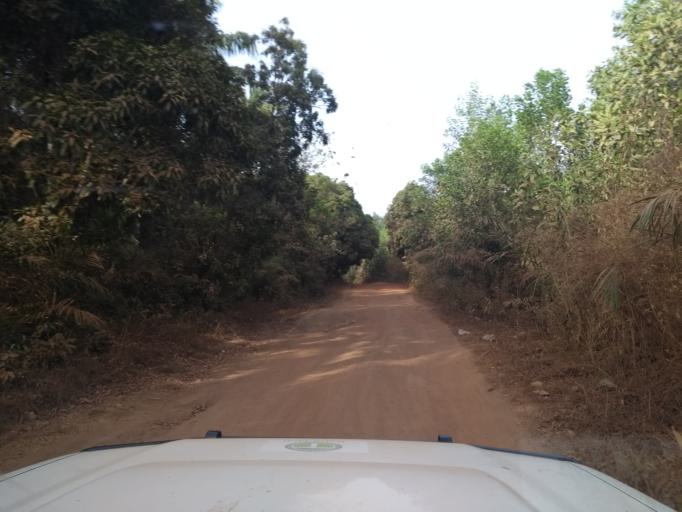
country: GN
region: Kindia
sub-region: Prefecture de Dubreka
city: Dubreka
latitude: 9.8578
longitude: -13.5482
